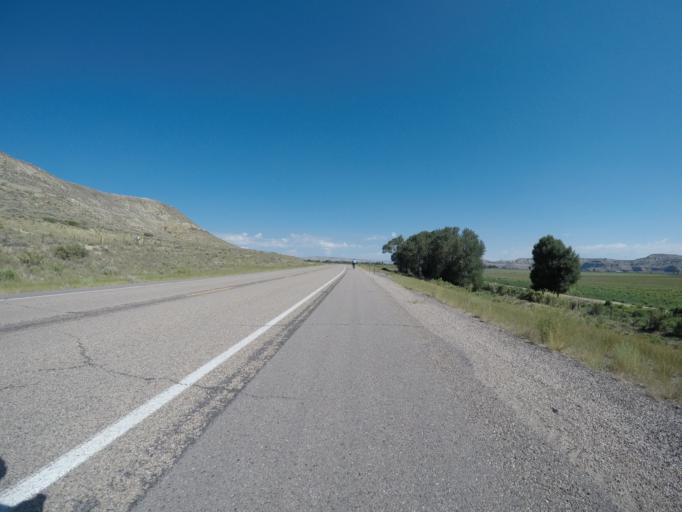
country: US
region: Wyoming
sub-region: Sublette County
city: Marbleton
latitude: 42.2015
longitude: -110.1796
